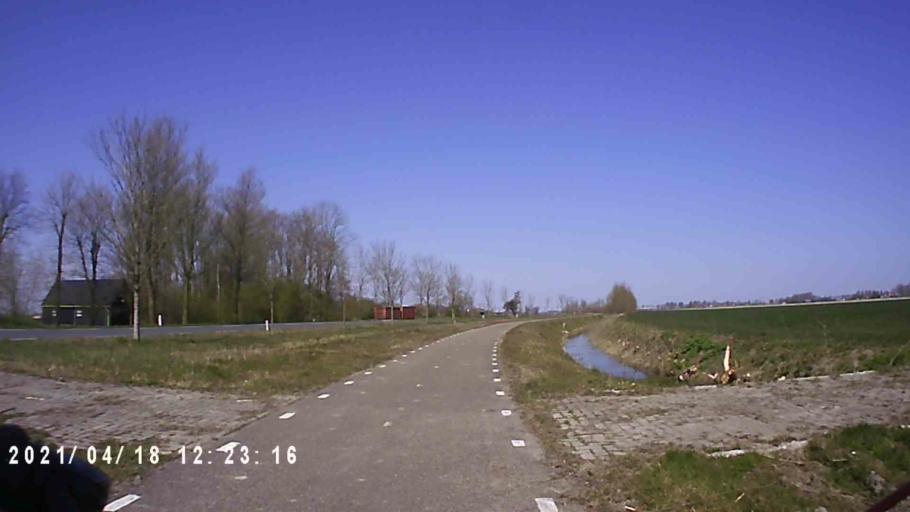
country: NL
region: Friesland
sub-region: Gemeente Dongeradeel
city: Anjum
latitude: 53.3248
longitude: 6.1227
